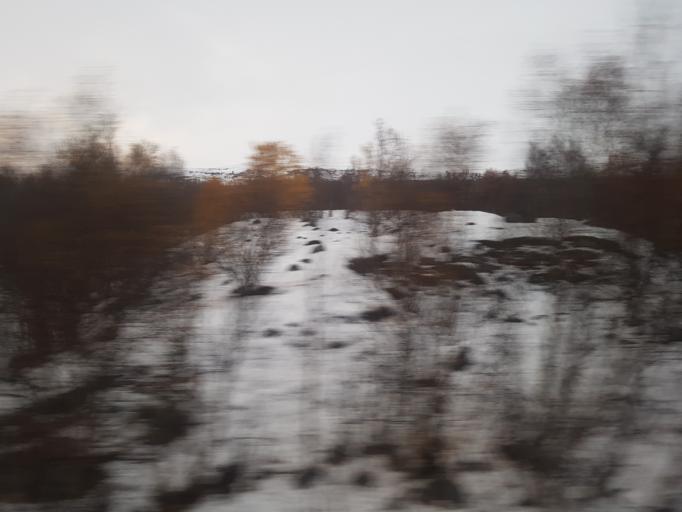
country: NO
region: Oppland
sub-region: Dovre
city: Dovre
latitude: 62.1679
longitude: 9.3883
